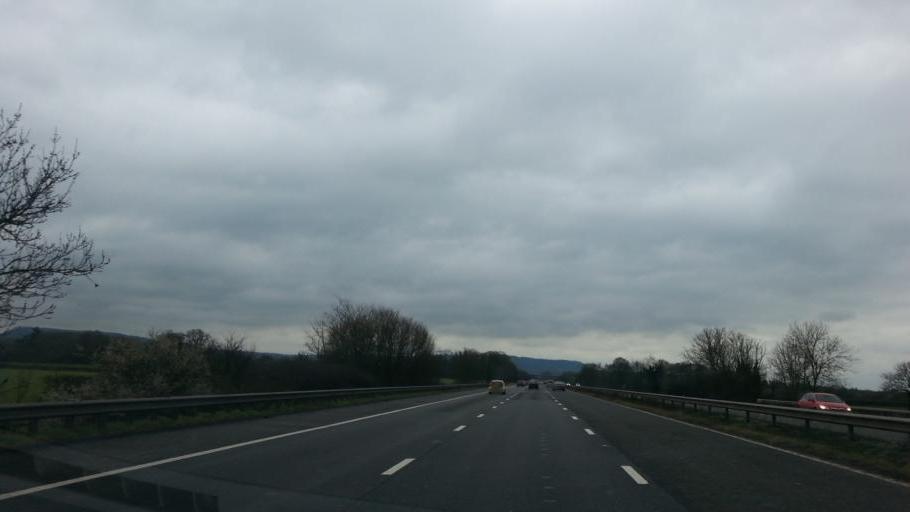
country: GB
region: England
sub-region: Gloucestershire
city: Dursley
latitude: 51.7393
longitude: -2.3415
